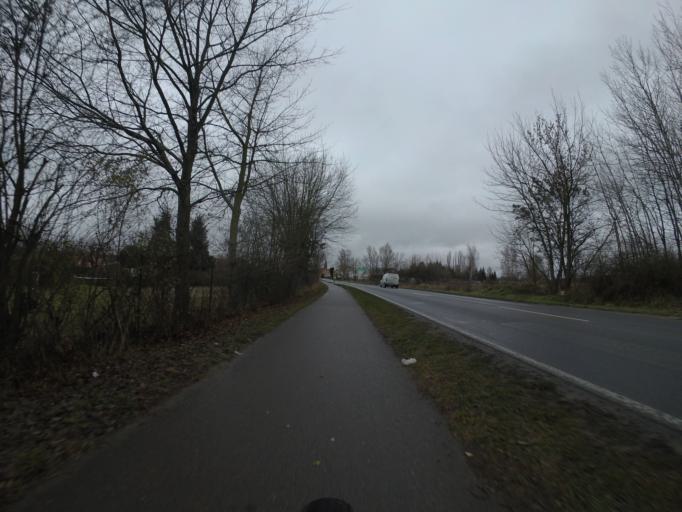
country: DE
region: Brandenburg
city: Ahrensfelde
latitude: 52.5580
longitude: 13.5910
